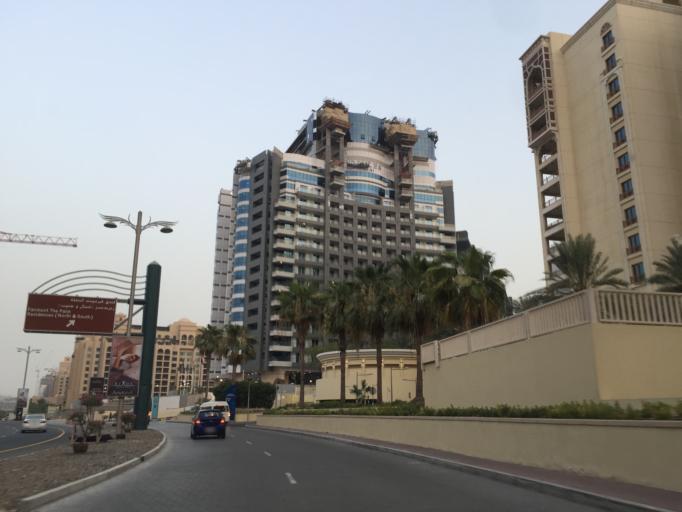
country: AE
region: Dubai
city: Dubai
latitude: 25.1135
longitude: 55.1370
